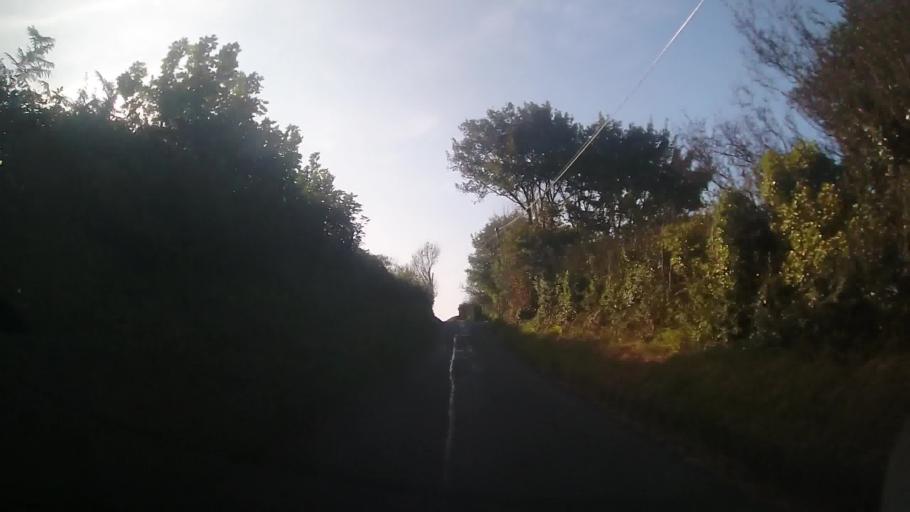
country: GB
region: Wales
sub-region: Pembrokeshire
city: Fishguard
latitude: 51.9824
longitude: -4.9432
